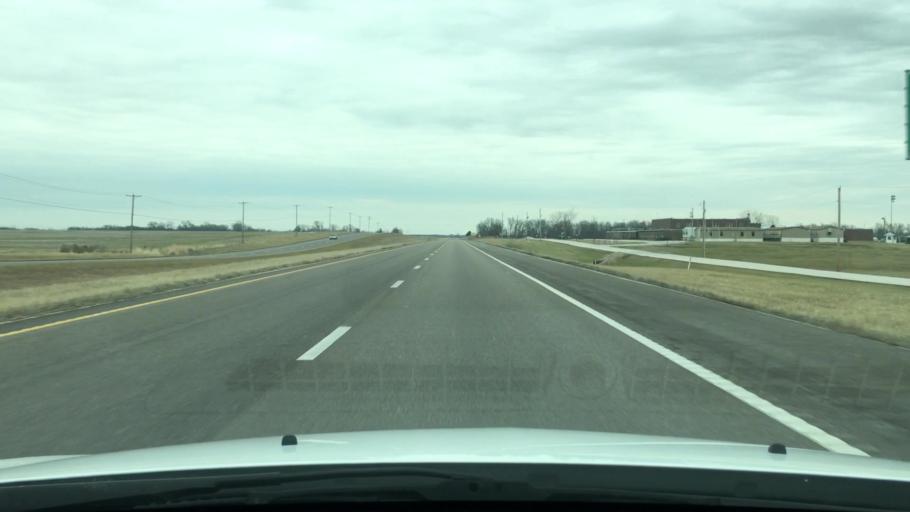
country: US
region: Missouri
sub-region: Callaway County
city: Fulton
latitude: 38.9605
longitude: -91.9235
